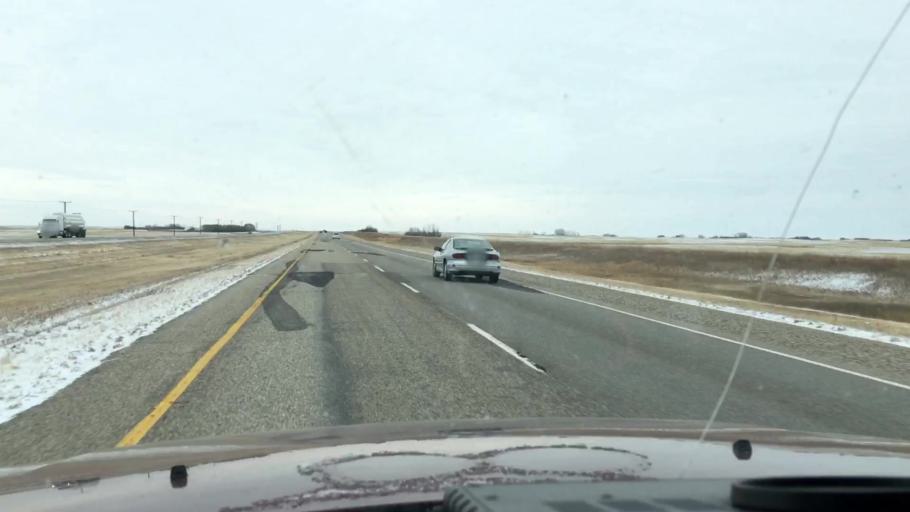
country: CA
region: Saskatchewan
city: Watrous
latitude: 51.4278
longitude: -106.1983
